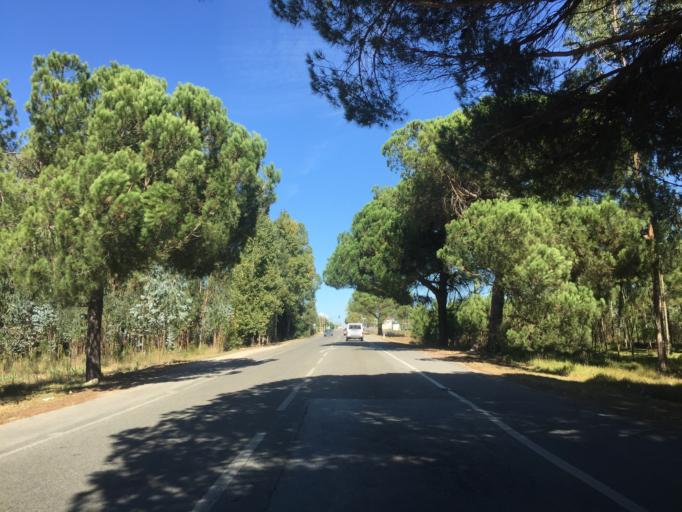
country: PT
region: Coimbra
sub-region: Figueira da Foz
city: Alhadas
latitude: 40.2957
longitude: -8.7631
